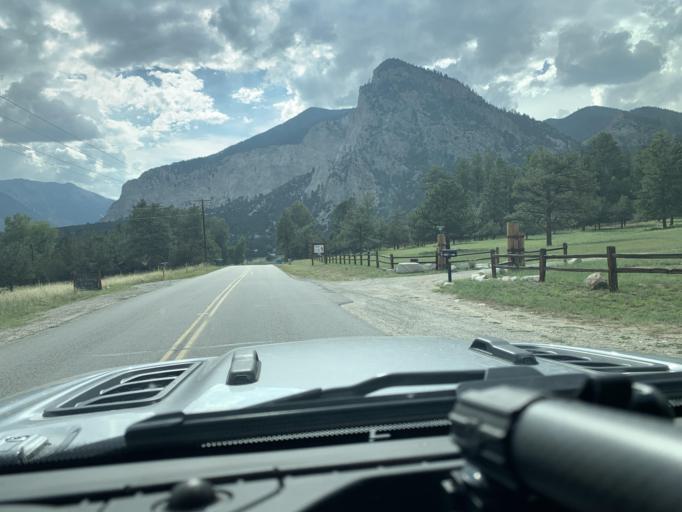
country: US
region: Colorado
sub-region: Chaffee County
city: Buena Vista
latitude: 38.7326
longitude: -106.1669
